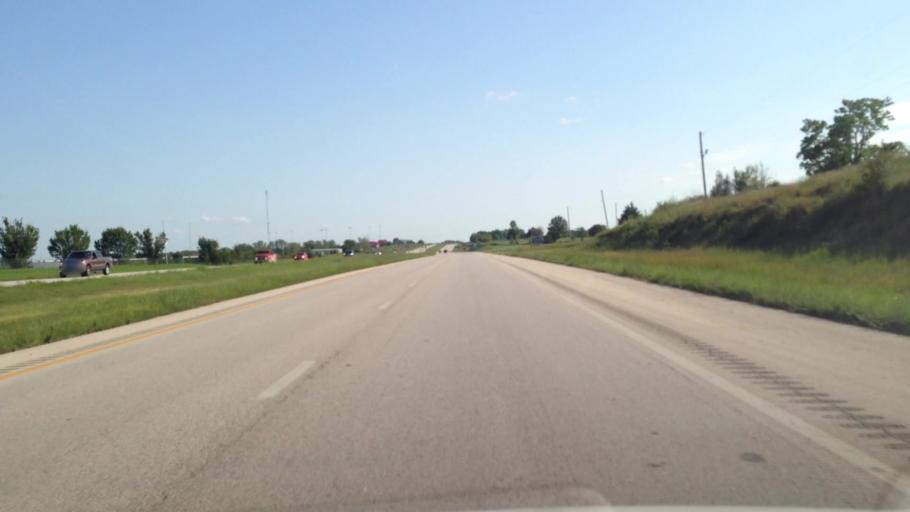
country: US
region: Kansas
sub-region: Bourbon County
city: Fort Scott
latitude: 37.7967
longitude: -94.7051
